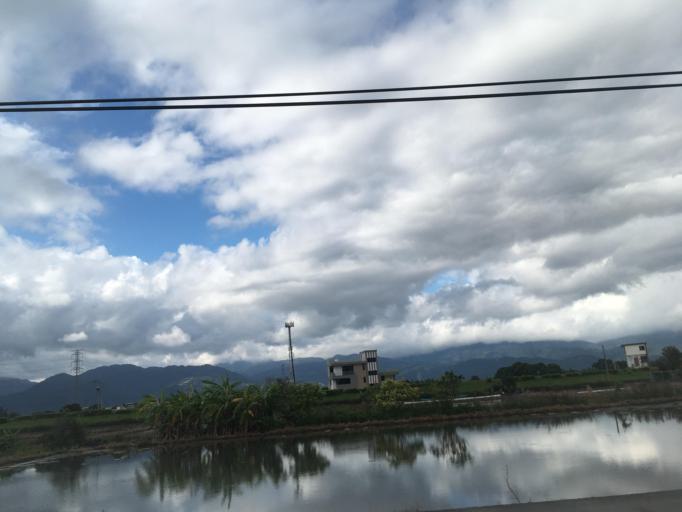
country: TW
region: Taiwan
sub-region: Yilan
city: Yilan
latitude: 24.6960
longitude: 121.7330
